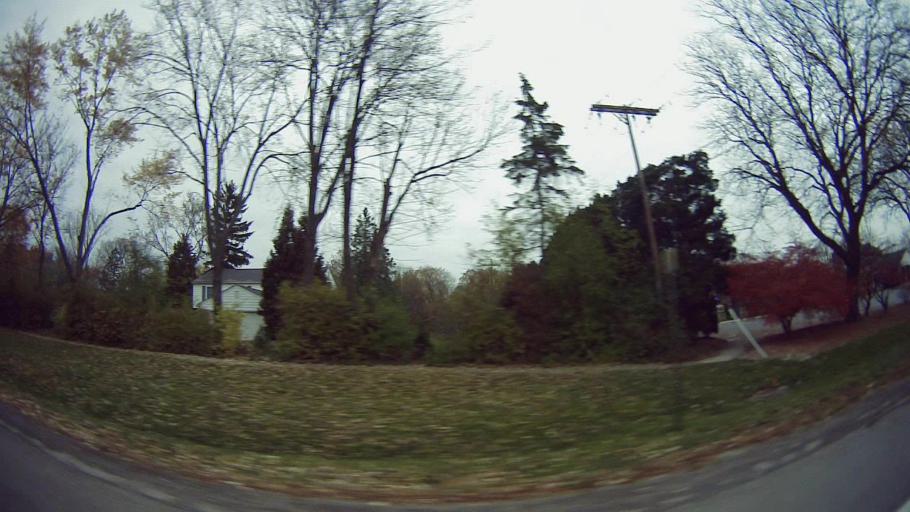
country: US
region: Michigan
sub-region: Oakland County
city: Bingham Farms
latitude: 42.5160
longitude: -83.2684
